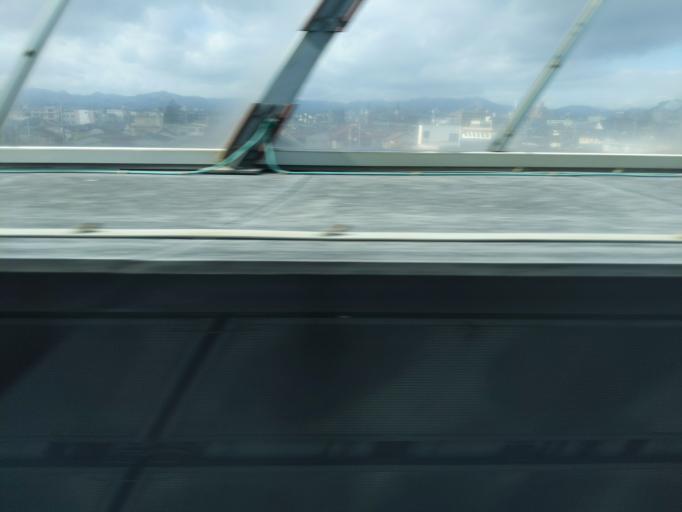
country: JP
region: Fukushima
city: Koriyama
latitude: 37.3806
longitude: 140.3843
